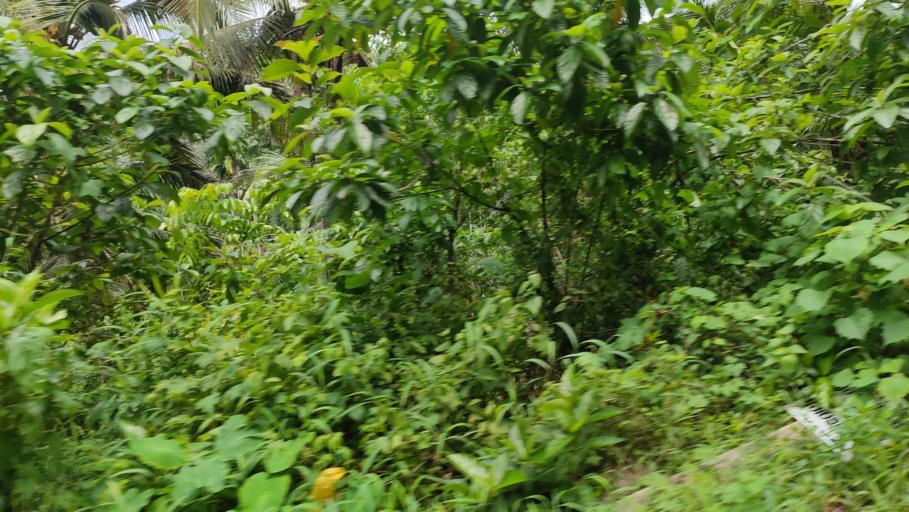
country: IN
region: Kerala
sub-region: Kasaragod District
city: Nileshwar
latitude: 12.2940
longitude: 75.2752
